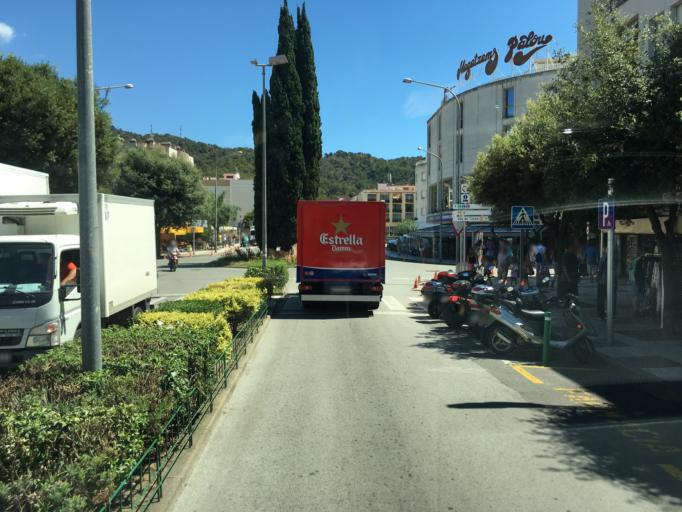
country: ES
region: Catalonia
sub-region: Provincia de Girona
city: Tossa de Mar
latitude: 41.7221
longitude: 2.9299
